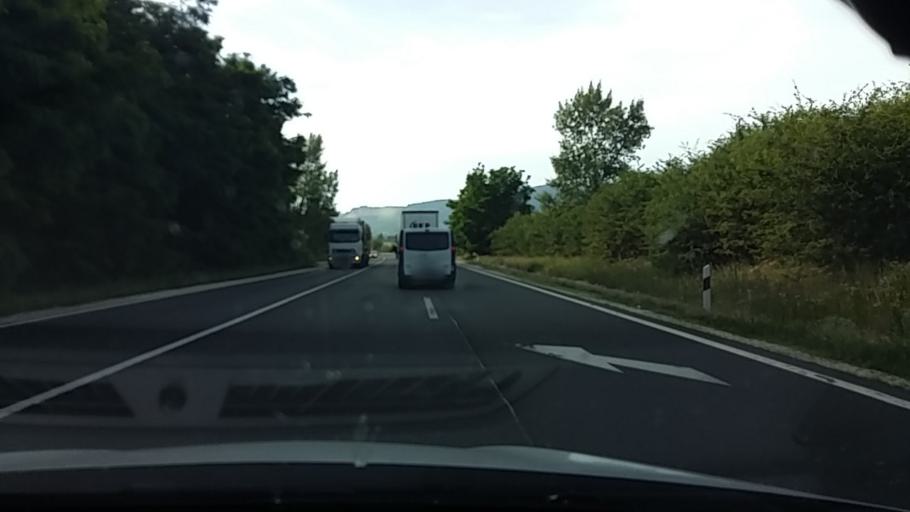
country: HU
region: Pest
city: Kosd
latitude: 47.7819
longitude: 19.1703
